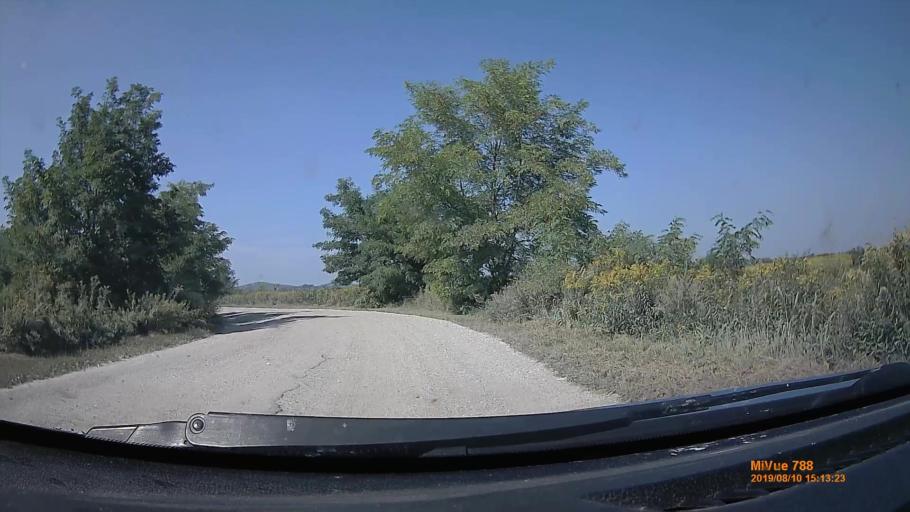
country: HU
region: Somogy
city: Fonyod
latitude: 46.6920
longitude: 17.5614
